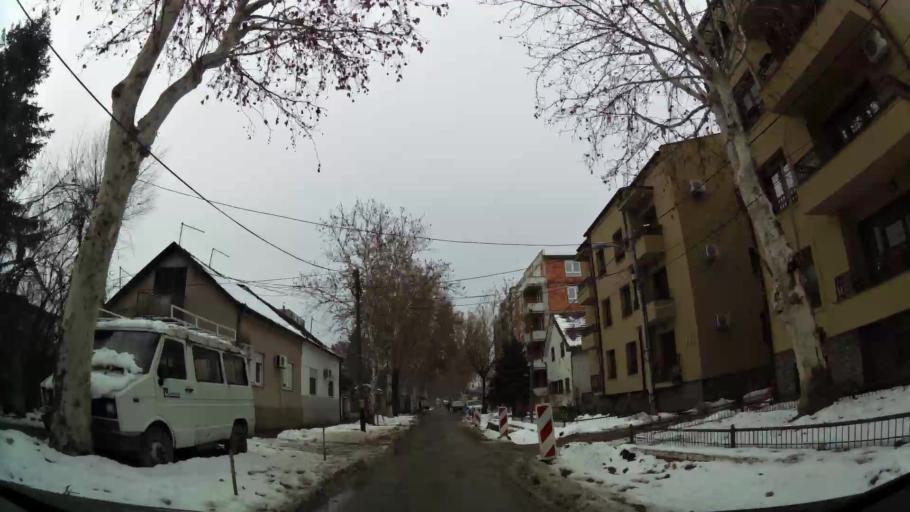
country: RS
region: Central Serbia
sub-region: Belgrade
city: Zemun
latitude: 44.8492
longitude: 20.3970
